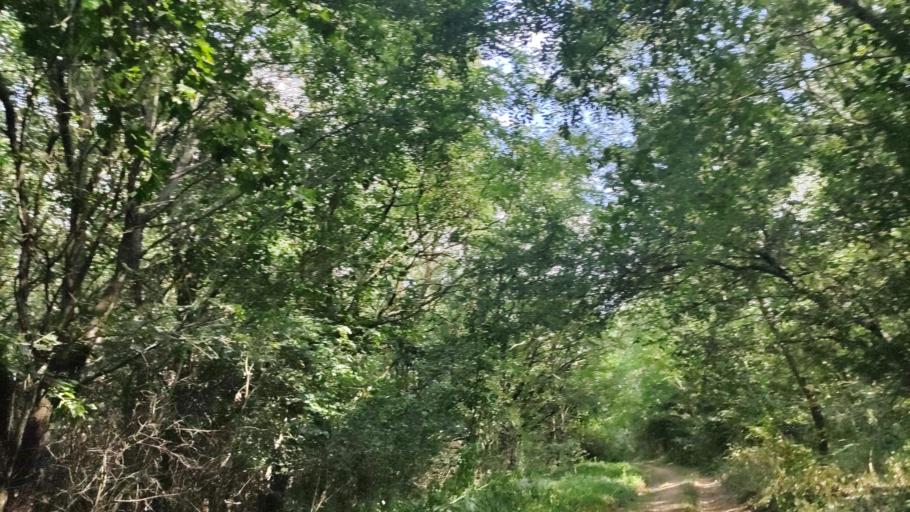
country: HU
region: Pest
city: Biatorbagy
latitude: 47.4673
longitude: 18.8588
